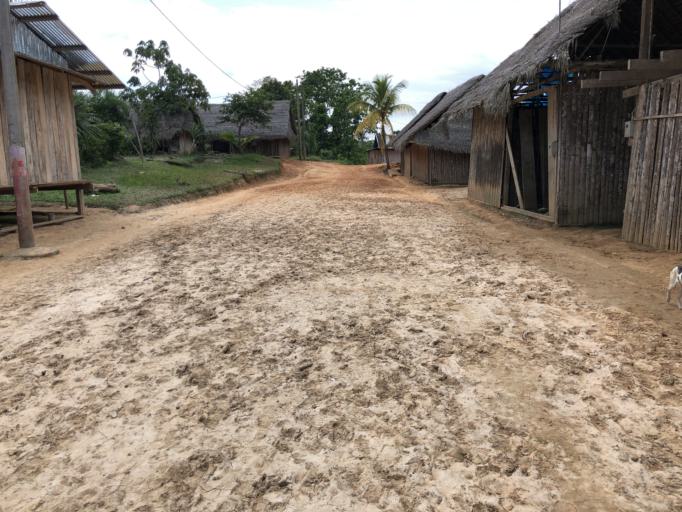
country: PE
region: Loreto
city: Puerto Galilea
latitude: -4.0548
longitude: -77.7574
